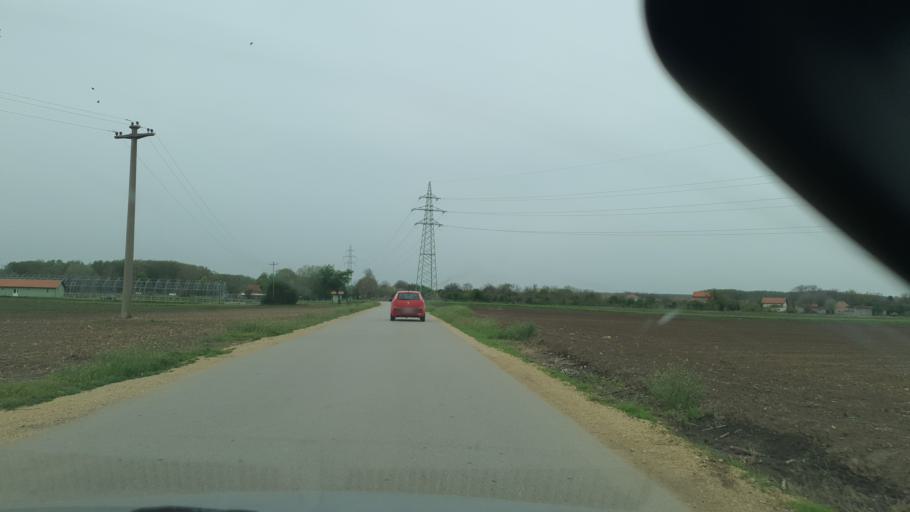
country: RS
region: Central Serbia
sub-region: Branicevski Okrug
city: Pozarevac
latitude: 44.7121
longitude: 21.1266
